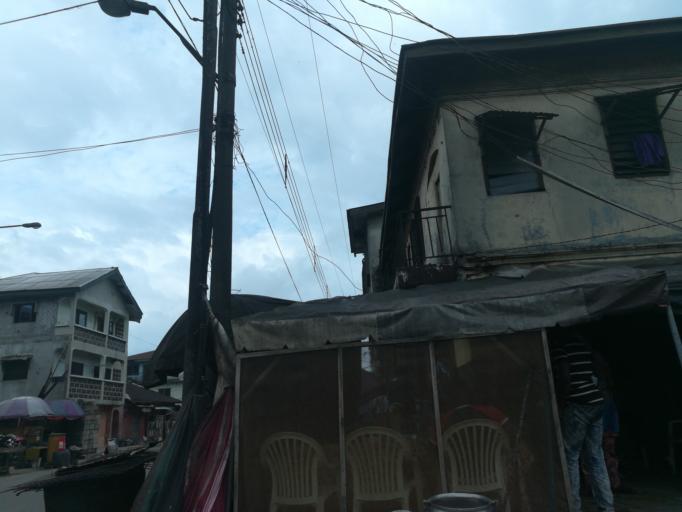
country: NG
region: Rivers
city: Port Harcourt
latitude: 4.7603
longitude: 7.0209
